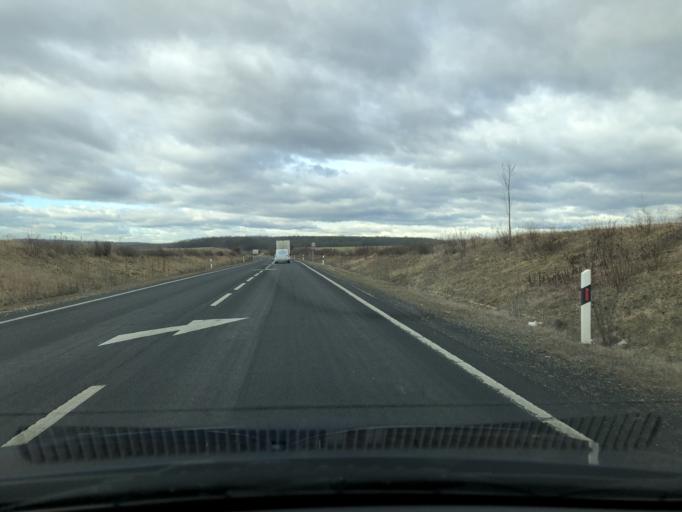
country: AT
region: Burgenland
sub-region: Politischer Bezirk Oberwart
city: Schachendorf
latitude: 47.2470
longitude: 16.5079
